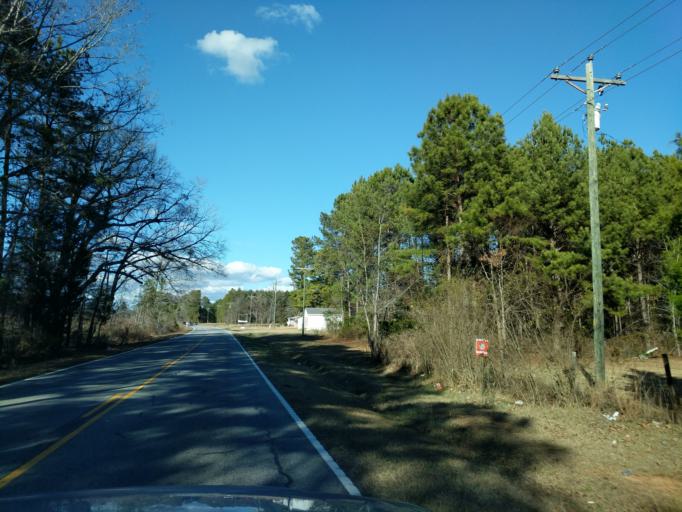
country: US
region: South Carolina
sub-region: Greenwood County
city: Ninety Six
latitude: 34.2962
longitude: -82.0461
